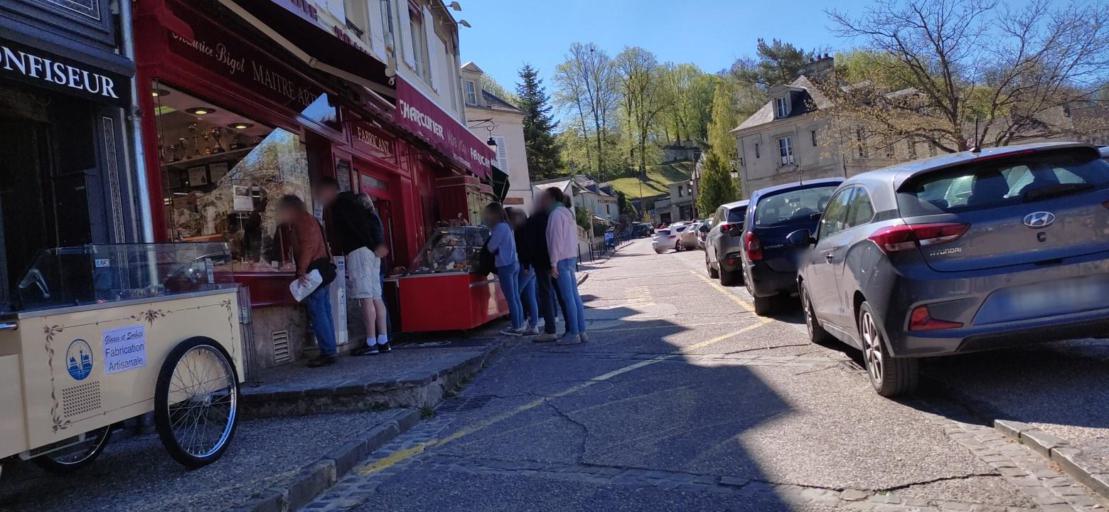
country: FR
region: Picardie
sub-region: Departement de l'Oise
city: Pierrefonds
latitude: 49.3478
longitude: 2.9781
